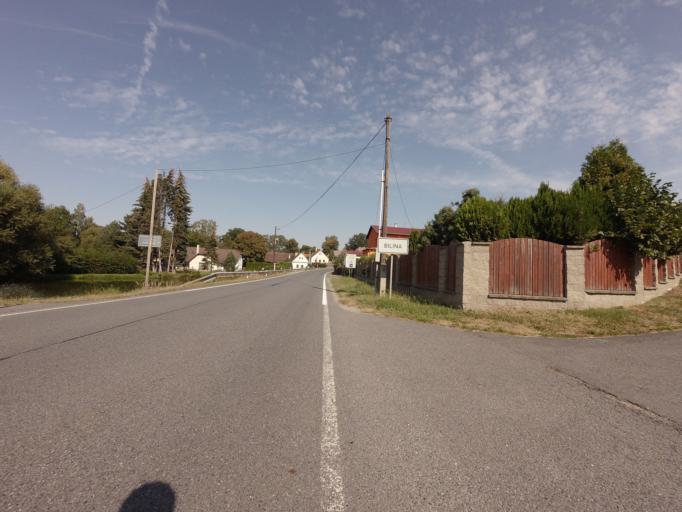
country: CZ
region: Jihocesky
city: Bernartice
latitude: 49.3802
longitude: 14.3672
